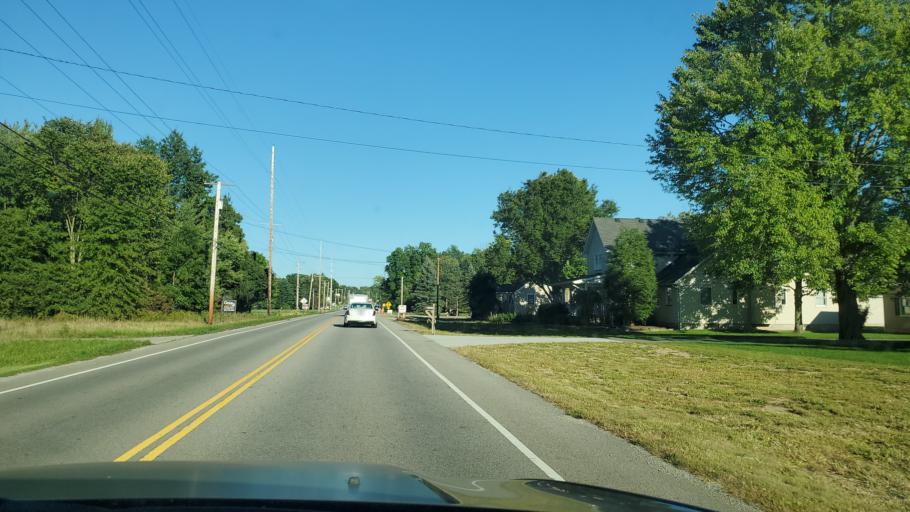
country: US
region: Ohio
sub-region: Mahoning County
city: Boardman
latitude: 40.9880
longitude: -80.6812
